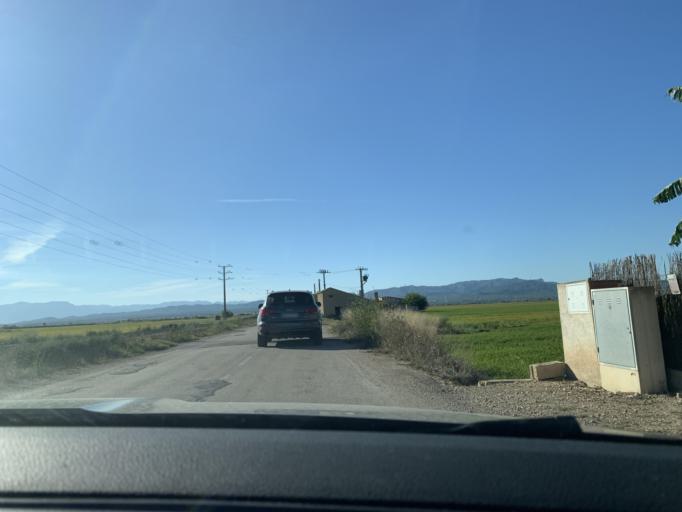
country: ES
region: Catalonia
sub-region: Provincia de Tarragona
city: Deltebre
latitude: 40.7497
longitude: 0.7253
